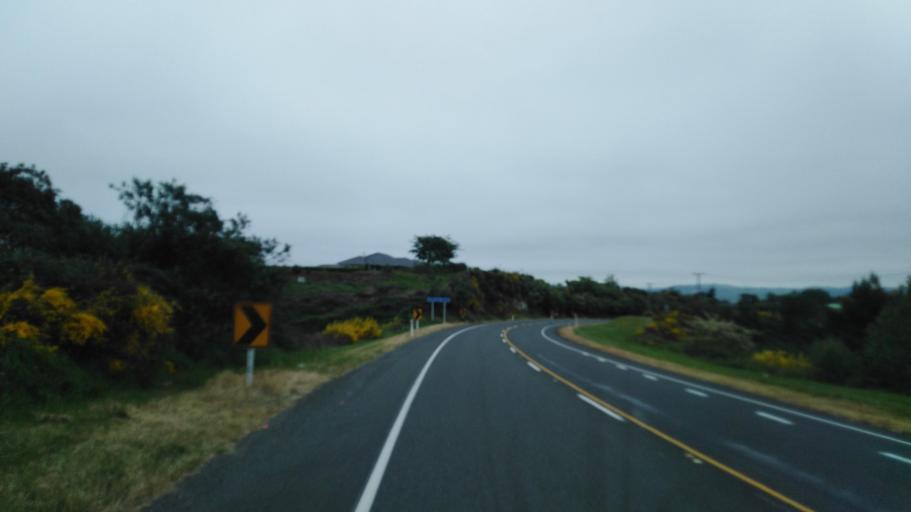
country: NZ
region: Waikato
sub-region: Taupo District
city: Taupo
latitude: -38.7059
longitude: 176.1037
